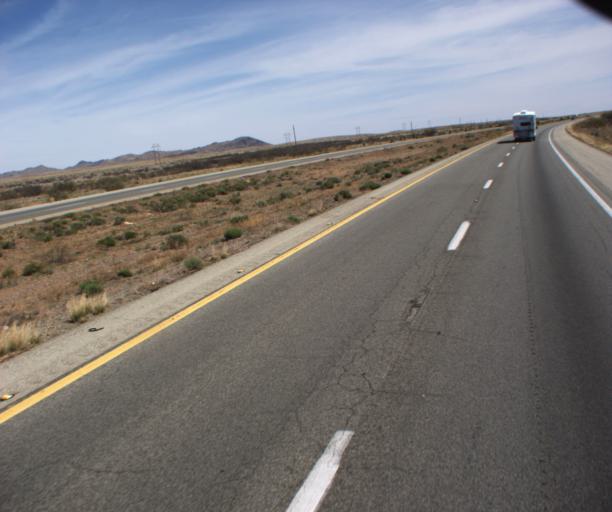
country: US
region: Arizona
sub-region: Cochise County
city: Willcox
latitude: 32.3441
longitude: -109.7509
